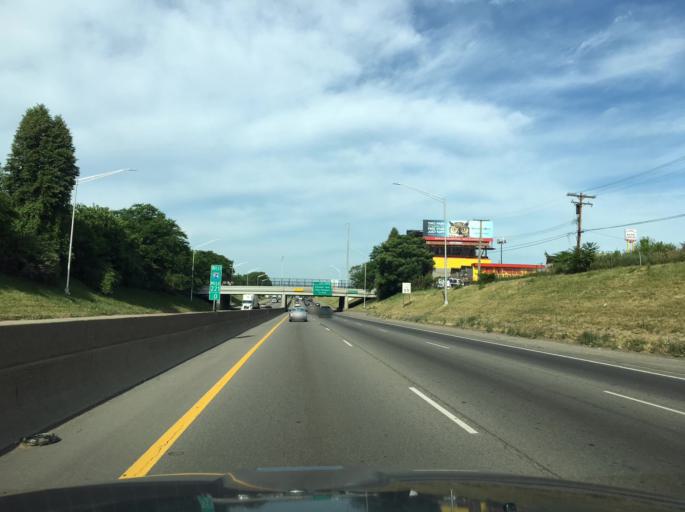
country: US
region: Michigan
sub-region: Wayne County
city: Grosse Pointe Park
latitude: 42.4021
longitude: -82.9711
